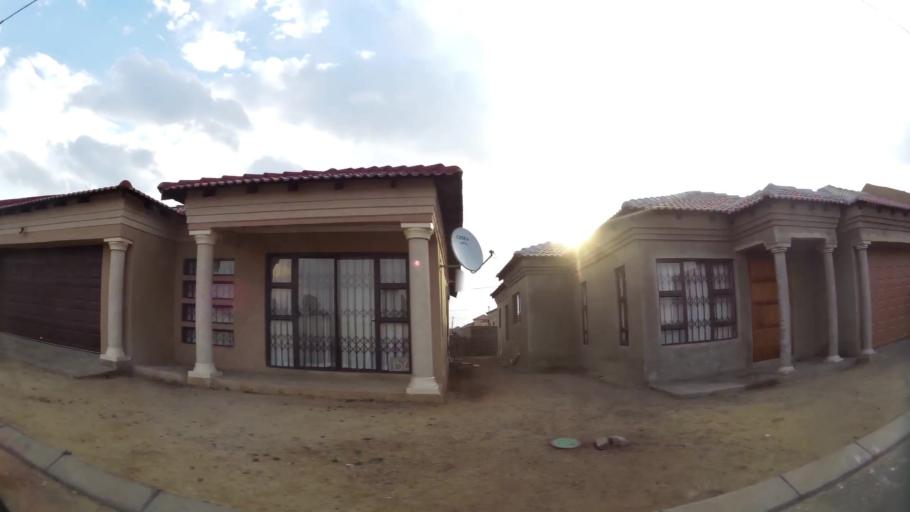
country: ZA
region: Gauteng
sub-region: Sedibeng District Municipality
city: Vanderbijlpark
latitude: -26.6095
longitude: 27.8149
